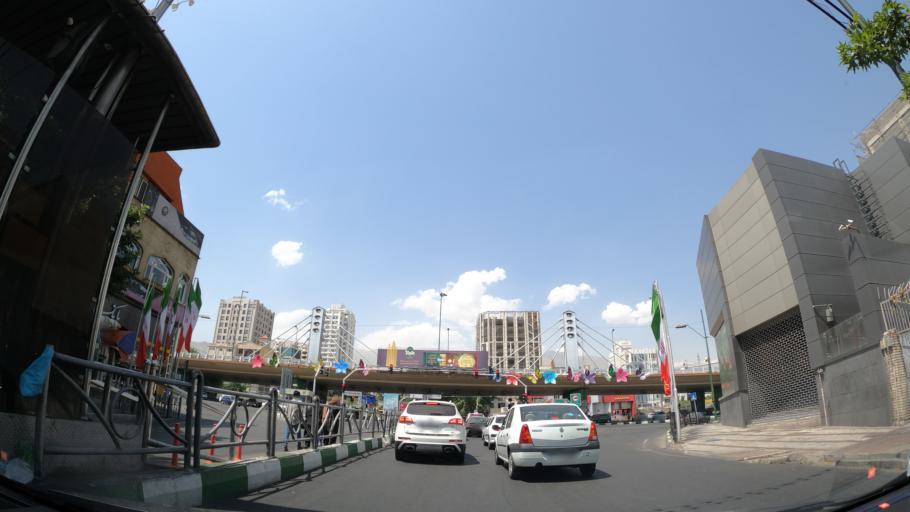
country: IR
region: Tehran
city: Tajrish
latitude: 35.7903
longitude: 51.4161
